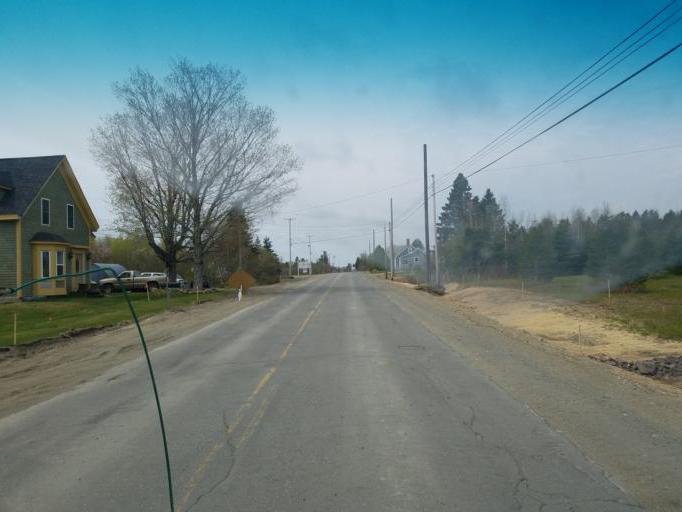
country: US
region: Maine
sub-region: Washington County
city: East Machias
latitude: 44.7890
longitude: -67.1814
